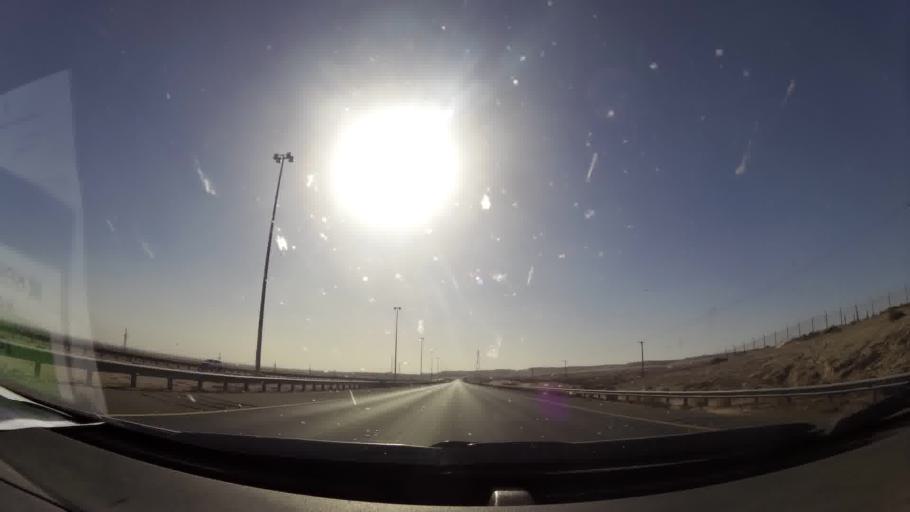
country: KW
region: Muhafazat al Jahra'
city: Al Jahra'
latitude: 29.4884
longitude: 47.7816
